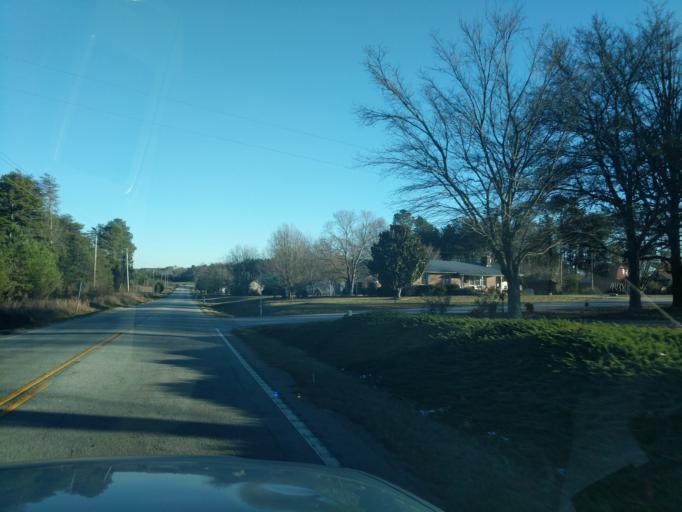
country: US
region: South Carolina
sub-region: Oconee County
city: Westminster
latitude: 34.6477
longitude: -83.0733
